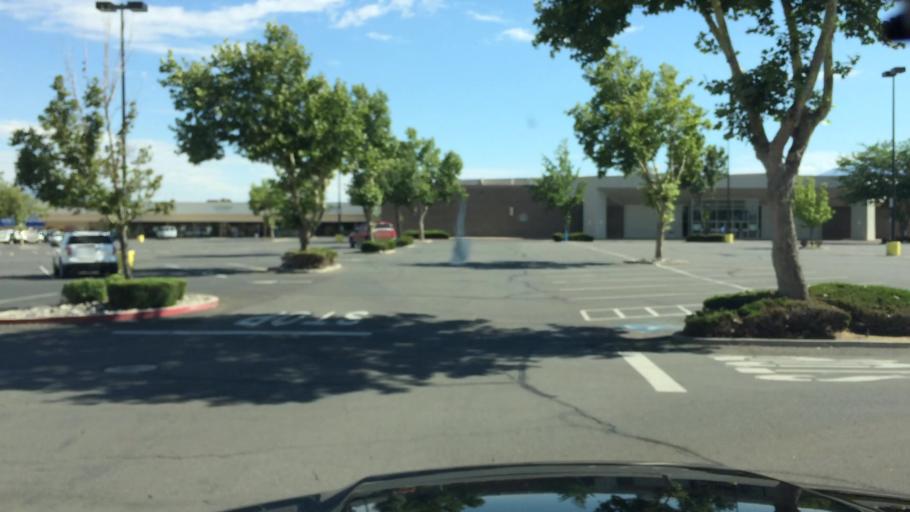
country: US
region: Nevada
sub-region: Washoe County
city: Reno
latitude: 39.4921
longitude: -119.7878
